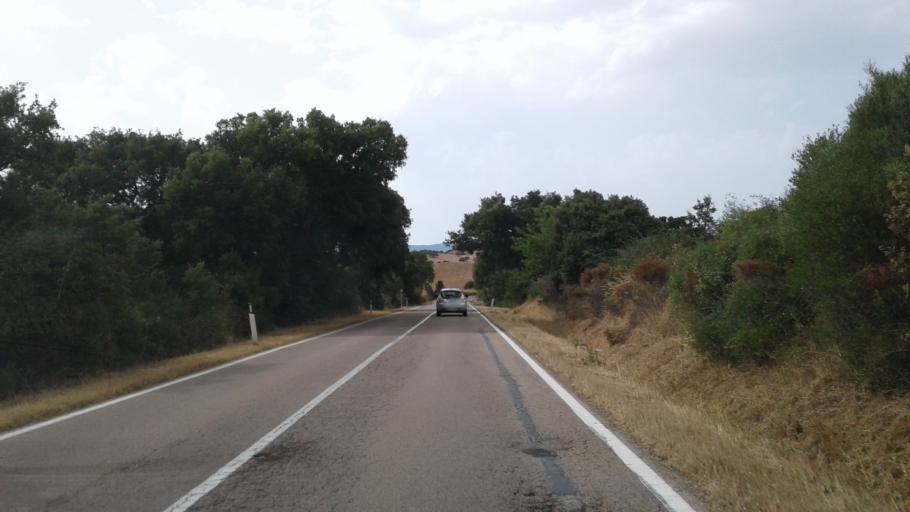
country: IT
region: Sardinia
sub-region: Provincia di Olbia-Tempio
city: Sant'Antonio di Gallura
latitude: 40.9448
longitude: 9.2998
